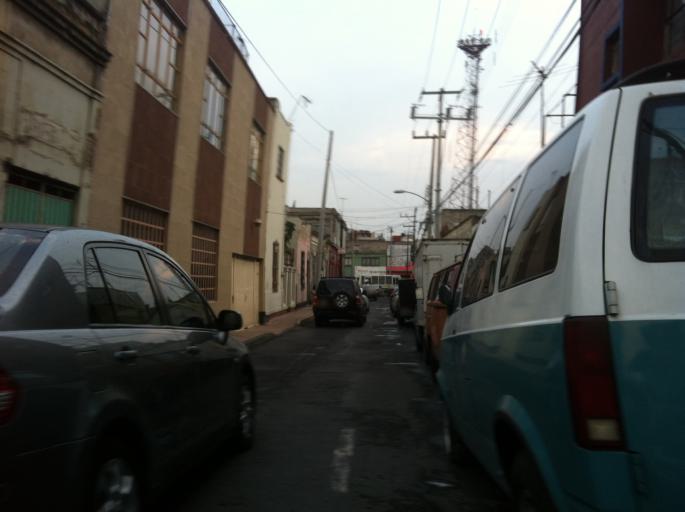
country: MX
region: Mexico City
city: Azcapotzalco
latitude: 19.4594
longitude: -99.1820
